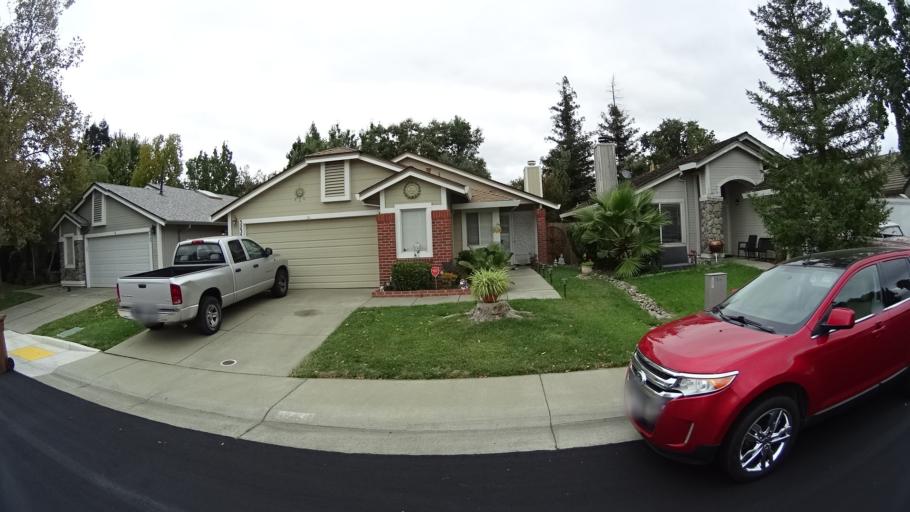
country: US
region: California
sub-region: Sacramento County
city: Laguna
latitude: 38.4244
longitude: -121.4433
